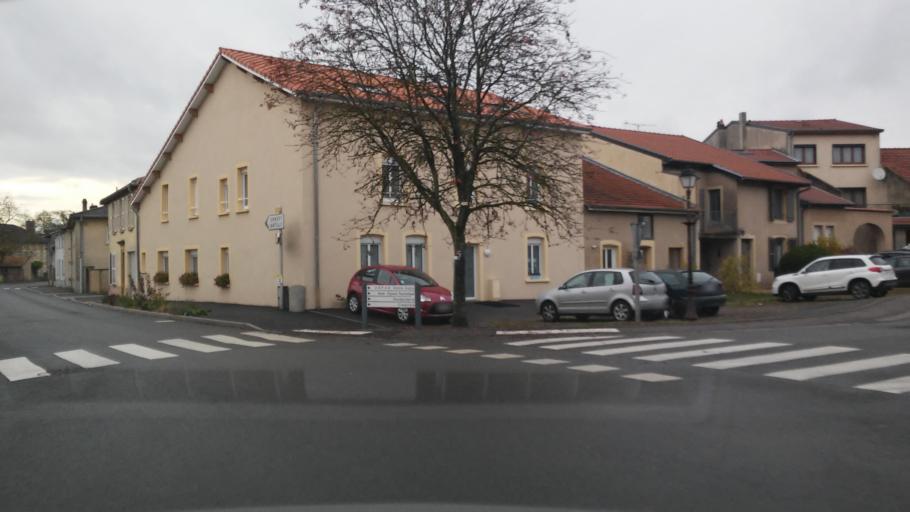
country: FR
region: Lorraine
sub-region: Departement de la Moselle
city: Vigy
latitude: 49.2033
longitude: 6.2965
